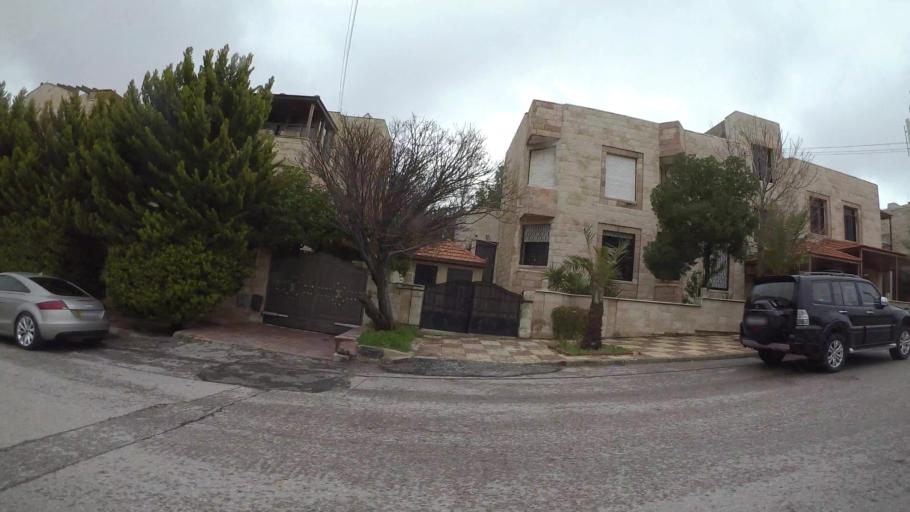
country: JO
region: Amman
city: Al Bunayyat ash Shamaliyah
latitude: 31.9435
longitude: 35.8847
